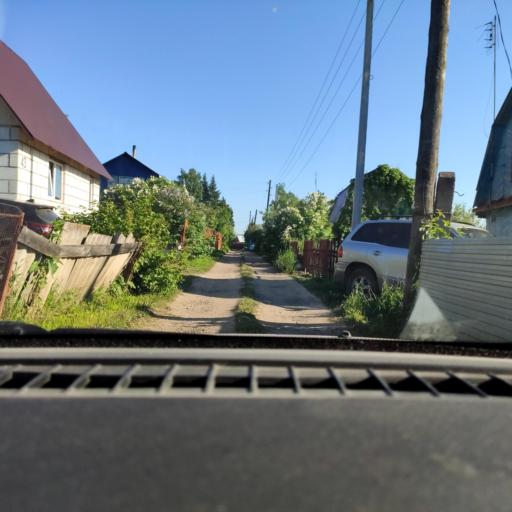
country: RU
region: Perm
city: Overyata
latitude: 58.1178
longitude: 55.8833
